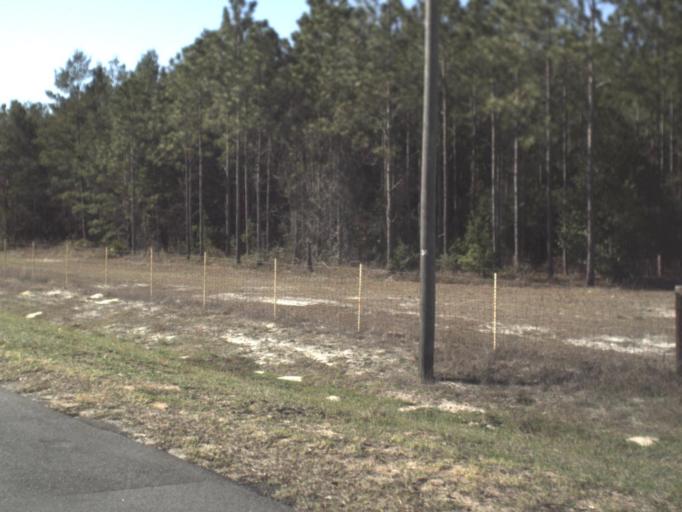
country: US
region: Florida
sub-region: Calhoun County
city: Blountstown
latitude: 30.4337
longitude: -85.2457
